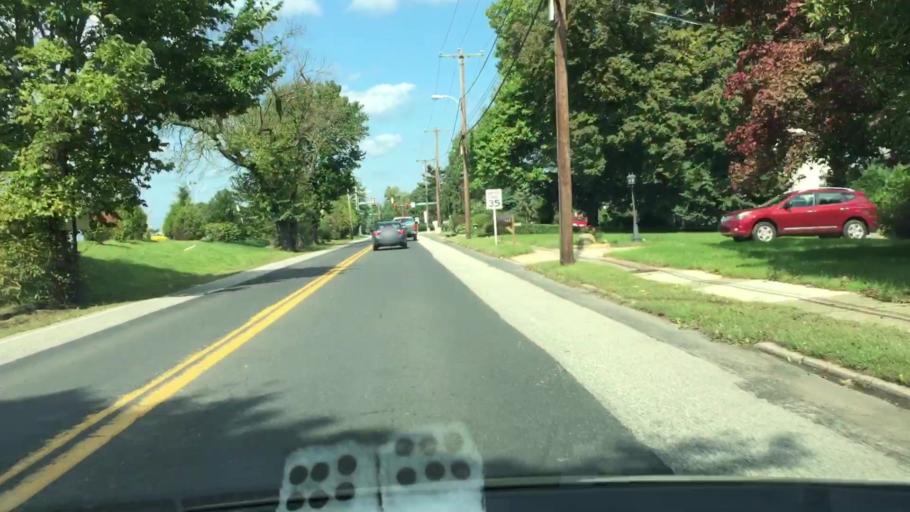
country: US
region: Pennsylvania
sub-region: Montgomery County
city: Norristown
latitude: 40.1193
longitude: -75.3070
